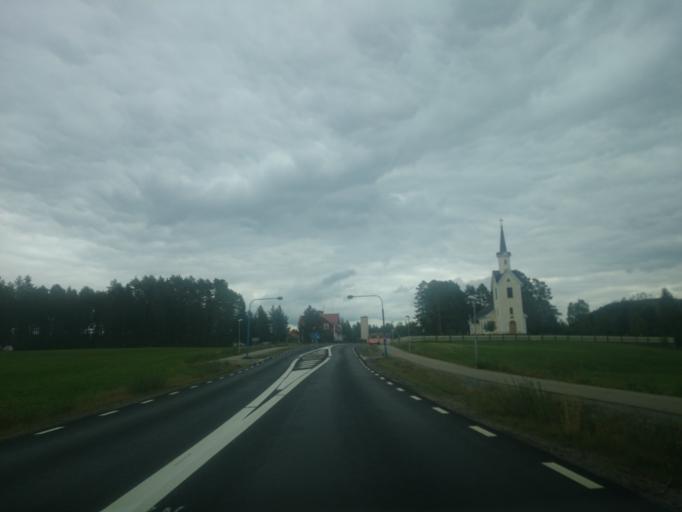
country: SE
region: Gaevleborg
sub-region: Ljusdals Kommun
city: Farila
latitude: 61.9838
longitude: 15.3098
